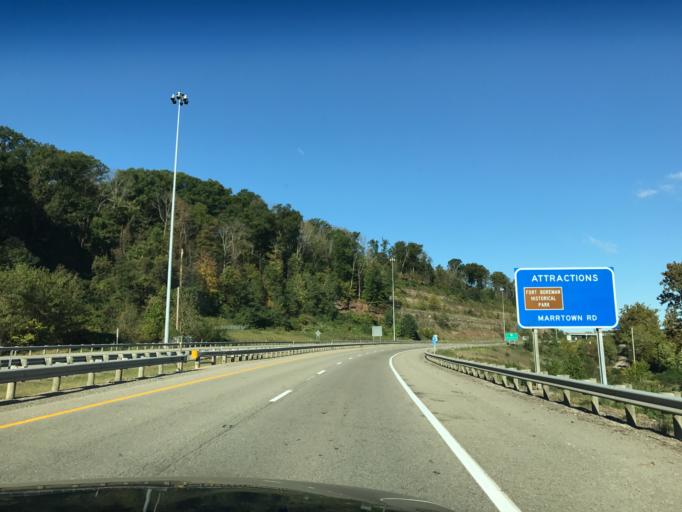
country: US
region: West Virginia
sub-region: Wood County
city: Parkersburg
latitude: 39.2595
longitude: -81.5622
